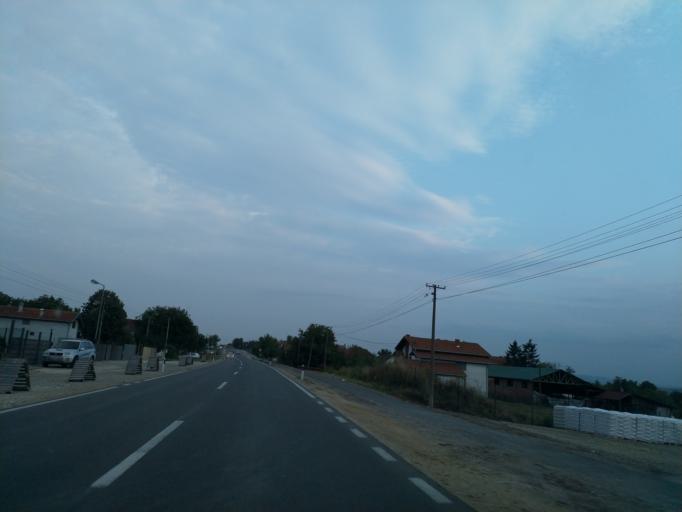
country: RS
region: Central Serbia
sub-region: Sumadijski Okrug
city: Kragujevac
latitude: 44.0838
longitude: 20.8680
